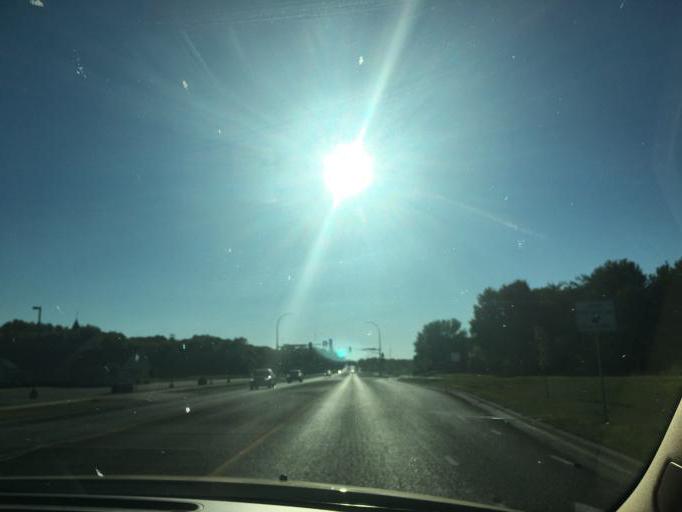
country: US
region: Minnesota
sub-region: Olmsted County
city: Rochester
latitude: 44.0795
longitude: -92.5273
